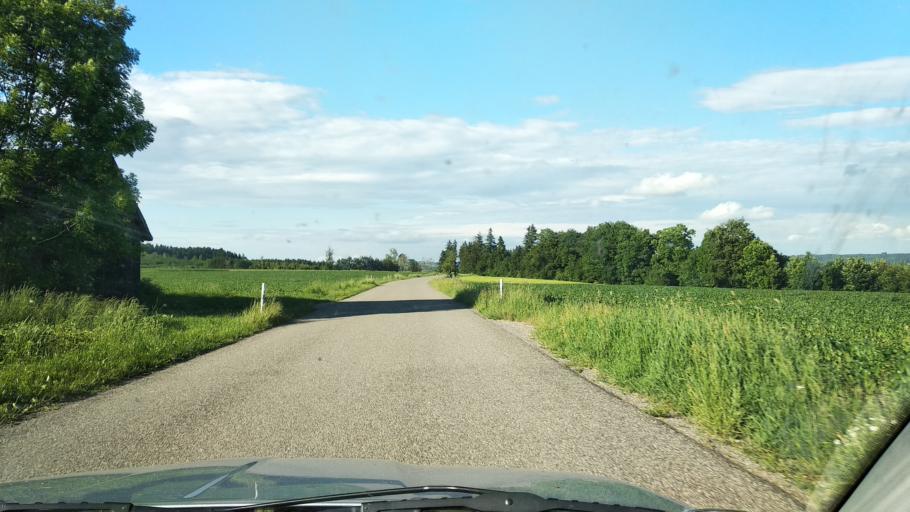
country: DE
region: Bavaria
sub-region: Swabia
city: Woringen
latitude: 47.8881
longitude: 10.1988
